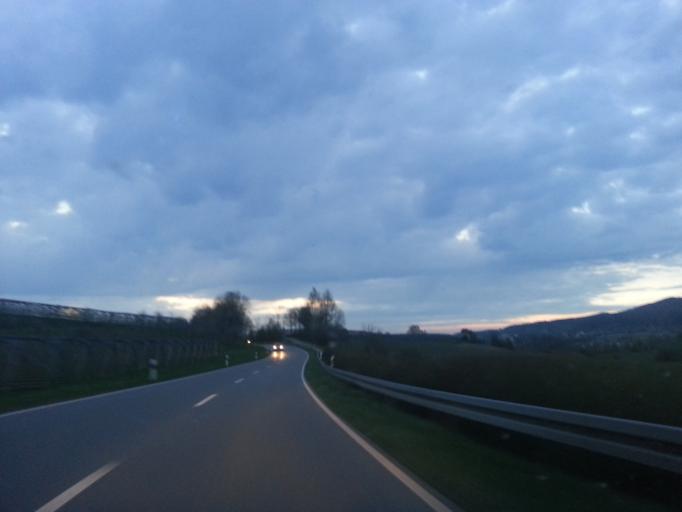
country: DE
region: Baden-Wuerttemberg
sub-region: Tuebingen Region
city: Markdorf
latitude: 47.7042
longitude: 9.4156
